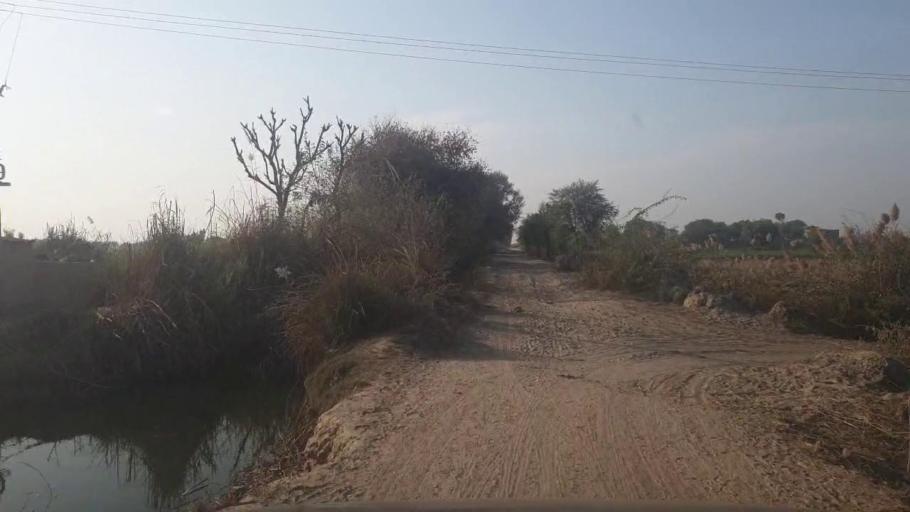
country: PK
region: Sindh
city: Sakrand
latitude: 26.0647
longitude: 68.3443
